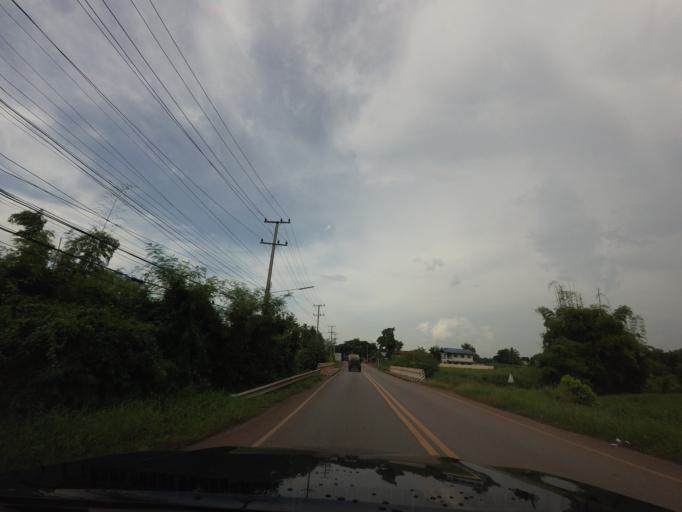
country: TH
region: Changwat Udon Thani
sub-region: Amphoe Ban Phue
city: Ban Phue
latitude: 17.6768
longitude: 102.4553
